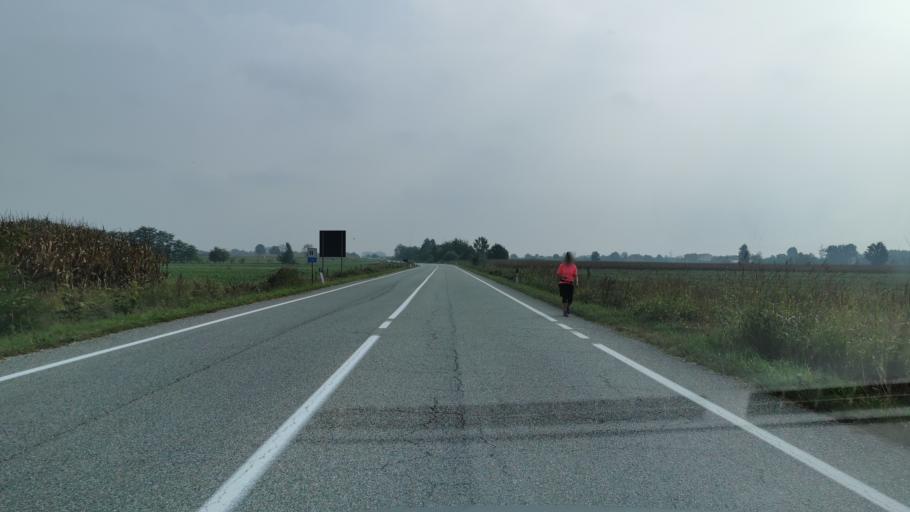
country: IT
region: Piedmont
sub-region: Provincia di Torino
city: Montanaro
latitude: 45.2312
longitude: 7.8677
